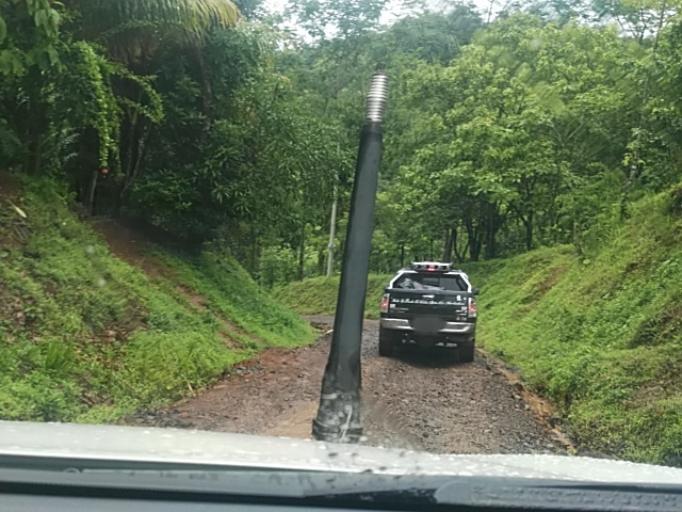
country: NI
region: Matagalpa
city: Rio Blanco
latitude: 13.0044
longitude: -85.2016
